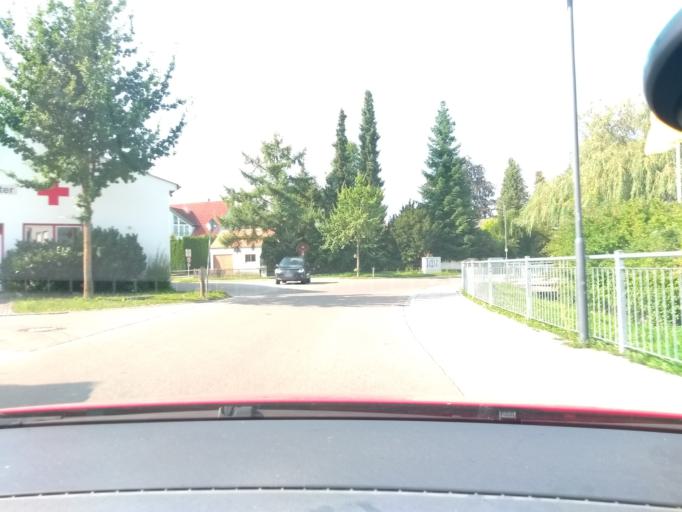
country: DE
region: Bavaria
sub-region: Upper Bavaria
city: Altomunster
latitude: 48.3872
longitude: 11.2529
